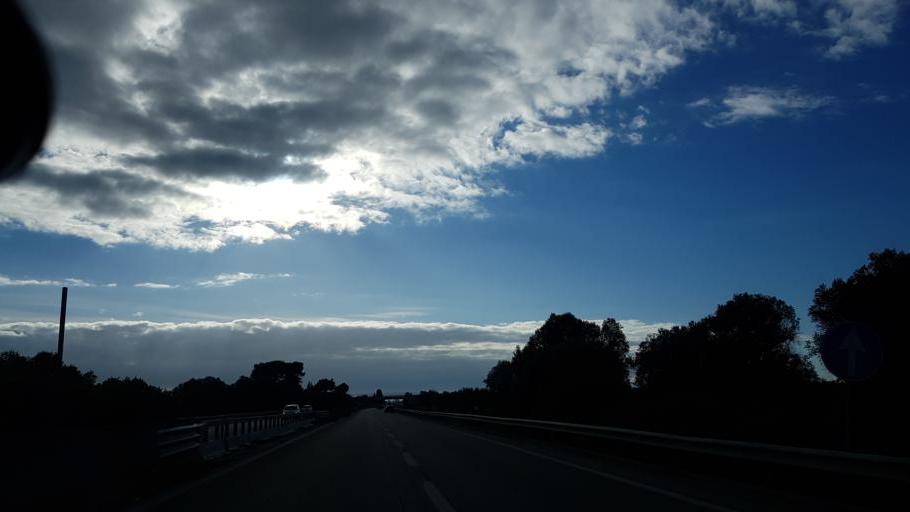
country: IT
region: Apulia
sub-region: Provincia di Brindisi
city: La Rosa
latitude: 40.5812
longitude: 17.9776
